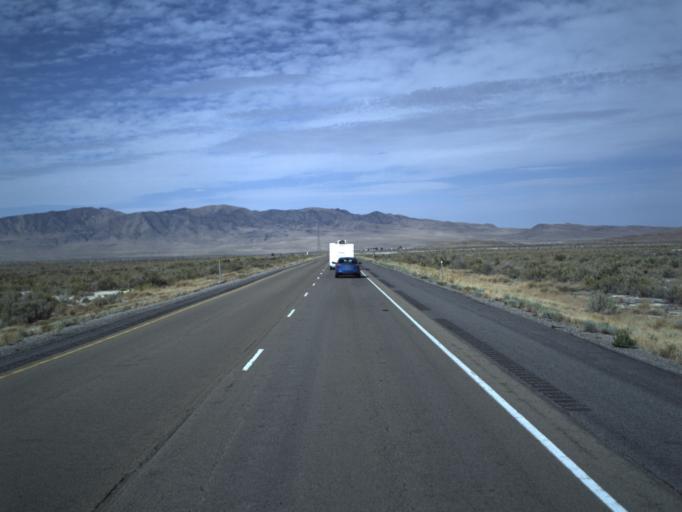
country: US
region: Utah
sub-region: Tooele County
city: Grantsville
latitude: 40.7547
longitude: -112.7391
